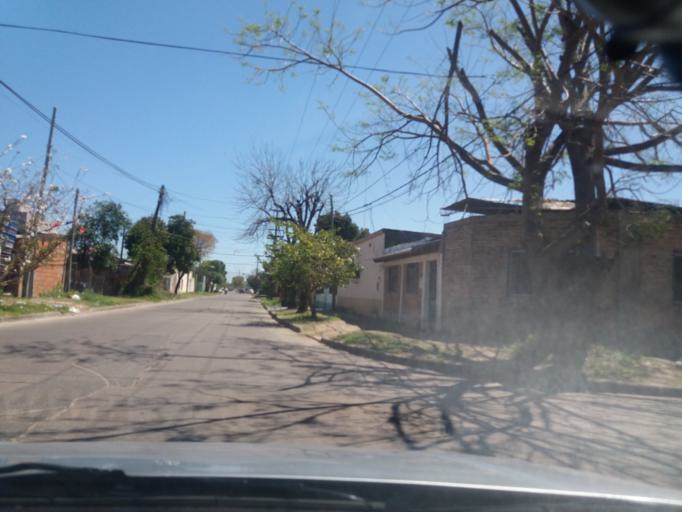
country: AR
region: Corrientes
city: Corrientes
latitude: -27.4894
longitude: -58.8362
